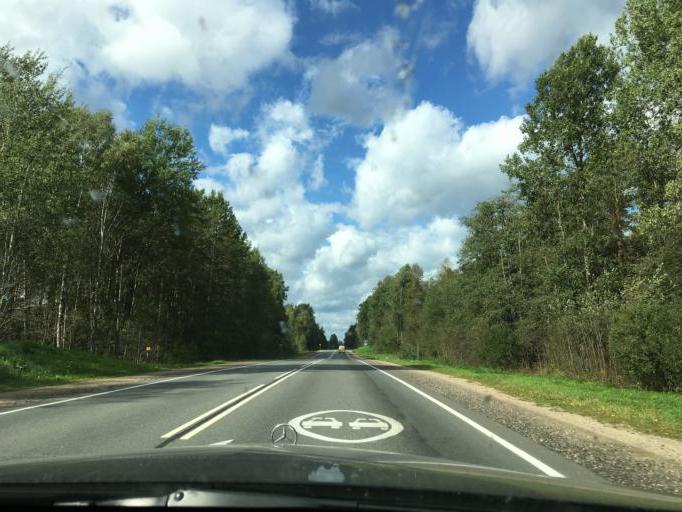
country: RU
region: Pskov
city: Pustoshka
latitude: 56.3871
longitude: 29.2555
